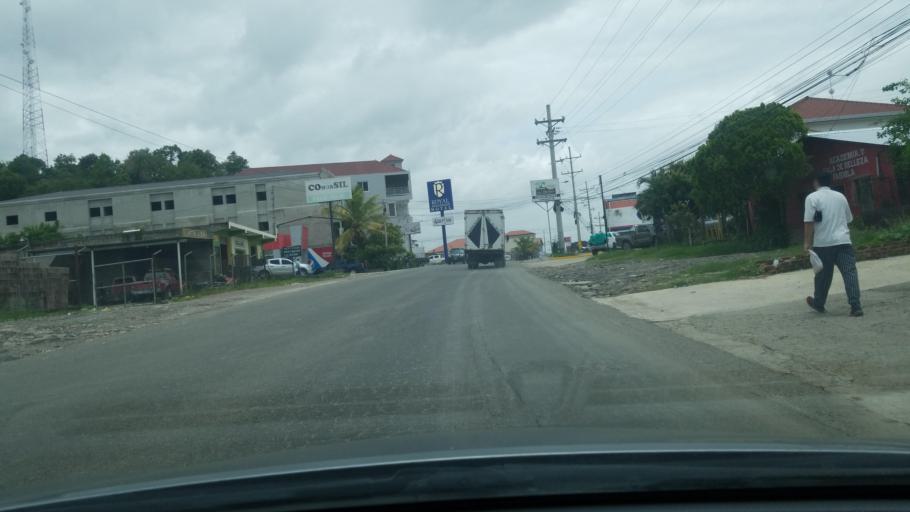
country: HN
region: Copan
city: Cucuyagua
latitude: 14.6583
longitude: -88.8724
